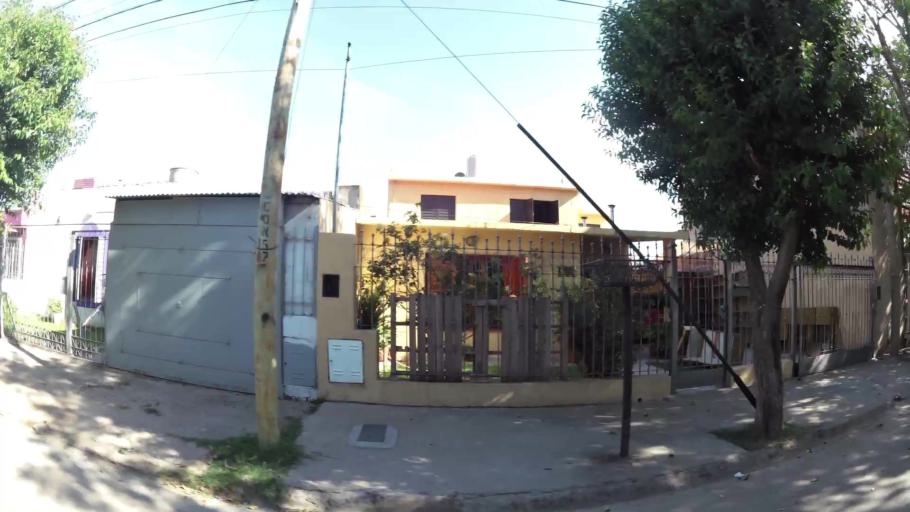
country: AR
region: Cordoba
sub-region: Departamento de Capital
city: Cordoba
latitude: -31.4405
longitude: -64.2120
